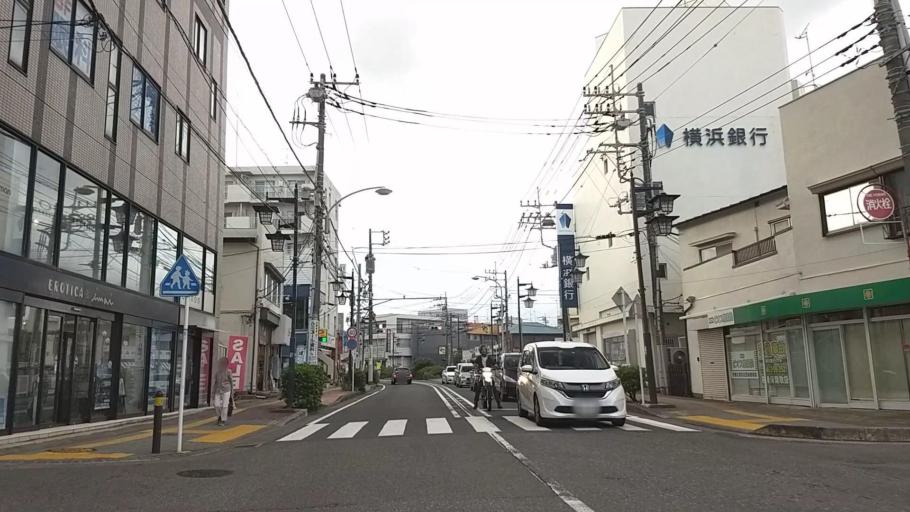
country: JP
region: Kanagawa
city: Isehara
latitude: 35.3955
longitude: 139.3122
